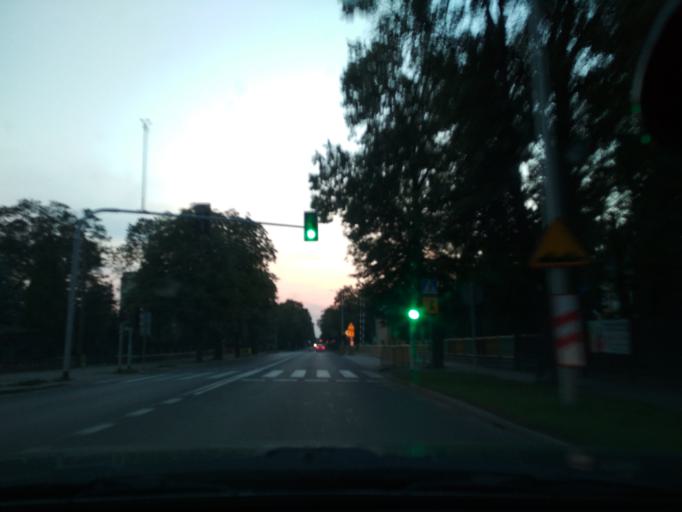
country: PL
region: Silesian Voivodeship
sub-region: Powiat zawiercianski
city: Zawiercie
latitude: 50.4801
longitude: 19.4420
